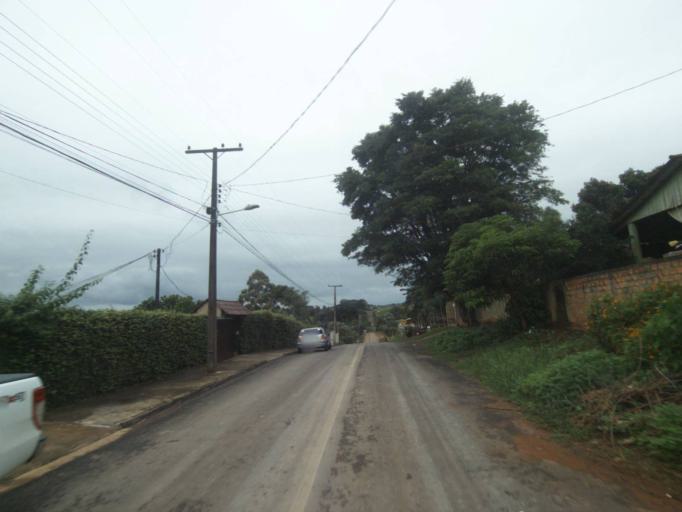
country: BR
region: Parana
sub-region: Telemaco Borba
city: Telemaco Borba
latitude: -24.3172
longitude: -50.6537
